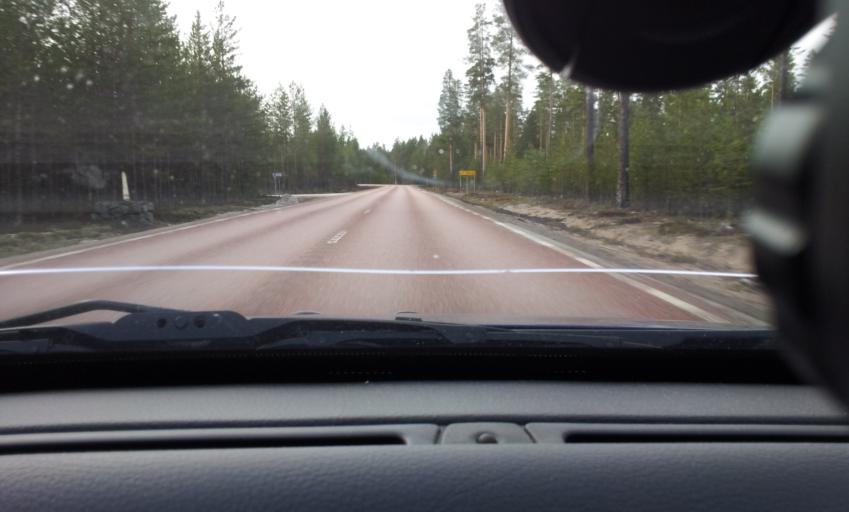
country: SE
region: Gaevleborg
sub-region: Ljusdals Kommun
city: Farila
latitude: 61.8963
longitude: 15.6545
